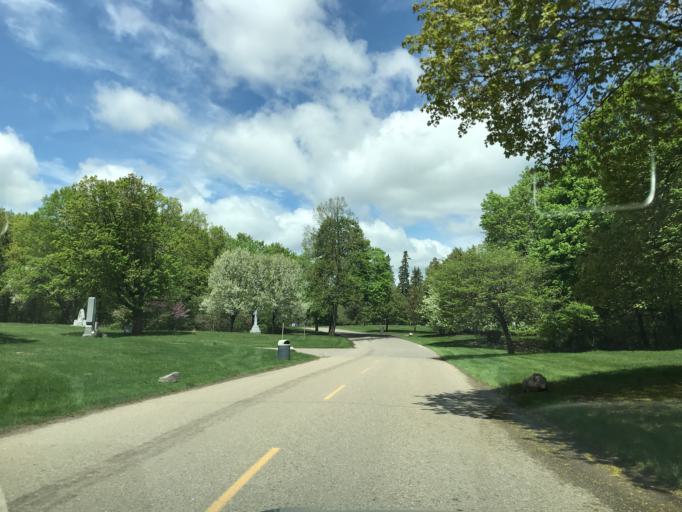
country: US
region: Michigan
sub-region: Oakland County
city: Franklin
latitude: 42.4808
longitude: -83.2999
